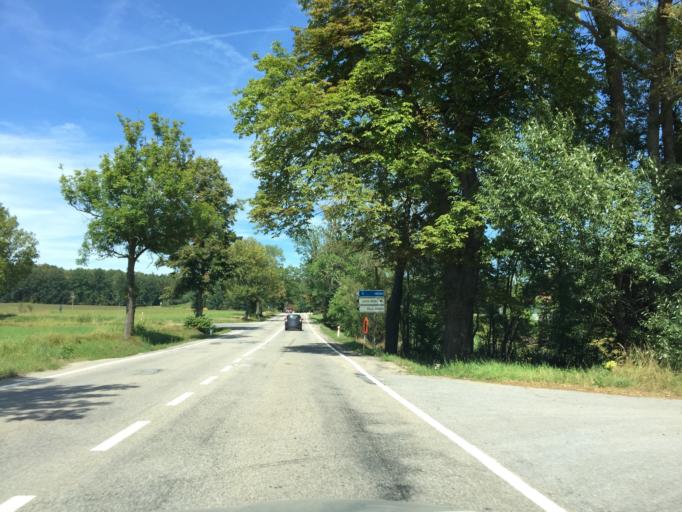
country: CZ
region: Jihocesky
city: Borek
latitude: 49.0435
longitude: 14.5070
